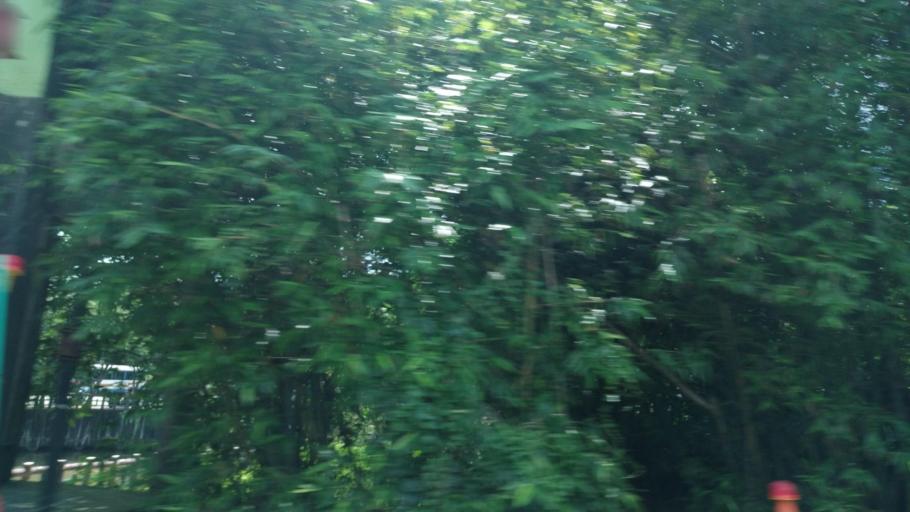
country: TW
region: Taipei
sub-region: Taipei
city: Banqiao
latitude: 24.9503
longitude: 121.5053
